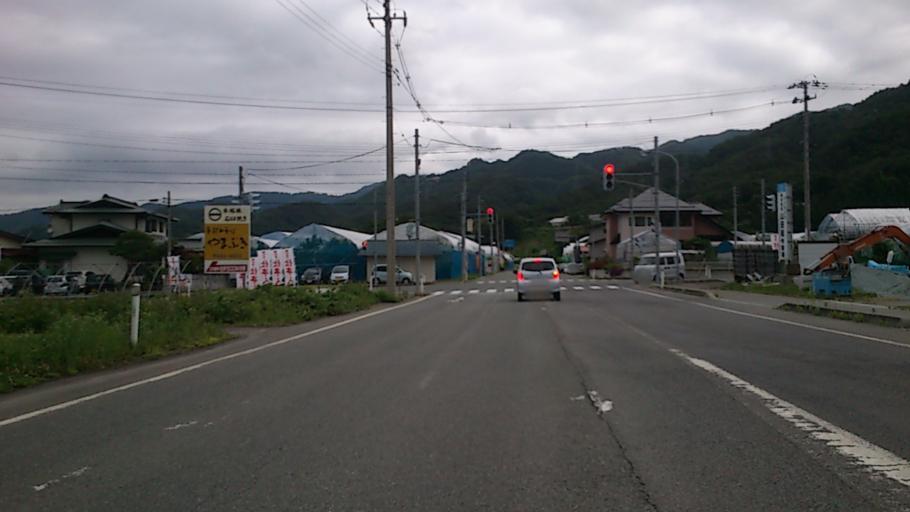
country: JP
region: Yamagata
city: Tendo
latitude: 38.3130
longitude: 140.4102
